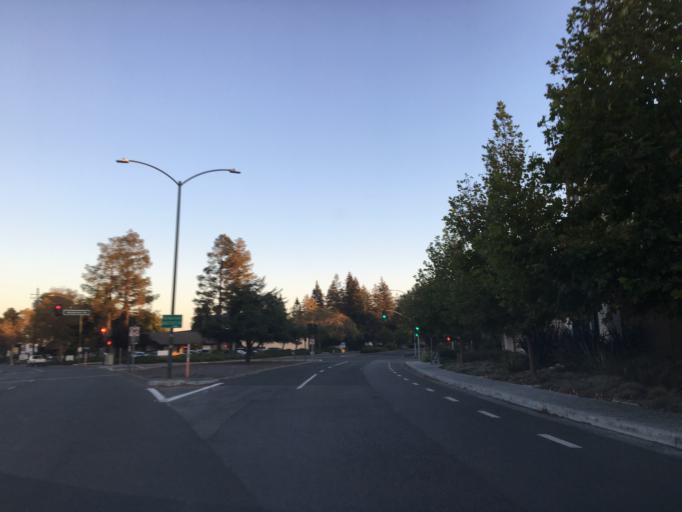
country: US
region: California
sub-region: Santa Clara County
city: Los Altos
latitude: 37.4151
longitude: -122.1013
